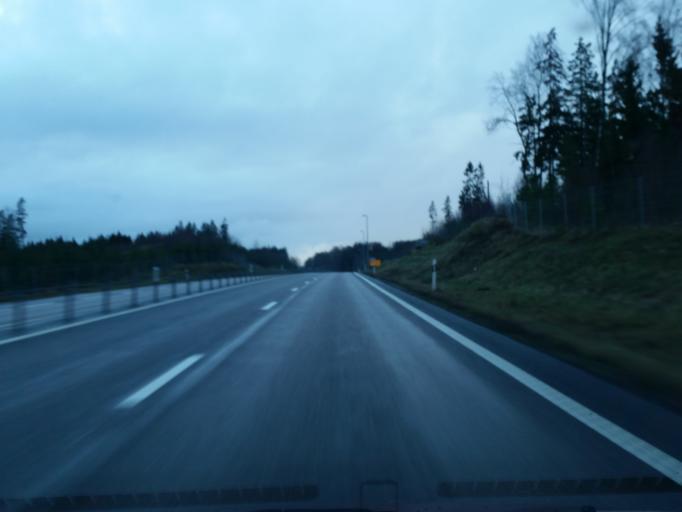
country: SE
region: Vaestra Goetaland
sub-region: Boras Kommun
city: Ganghester
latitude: 57.6728
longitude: 13.0015
